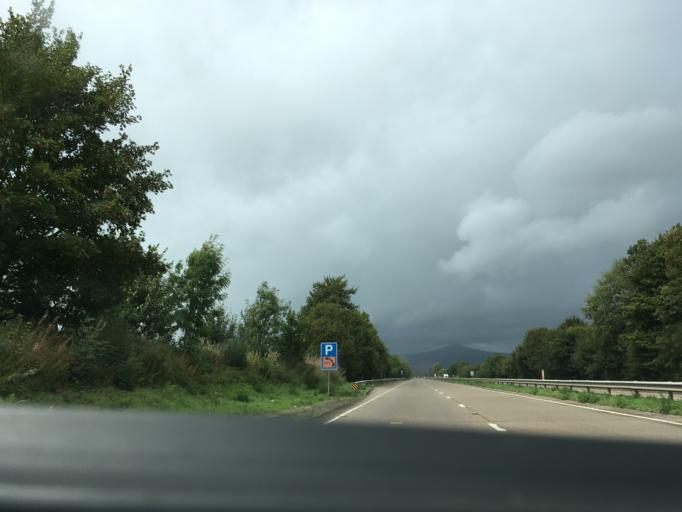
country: GB
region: Wales
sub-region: Monmouthshire
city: Abergavenny
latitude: 51.7938
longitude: -2.9942
